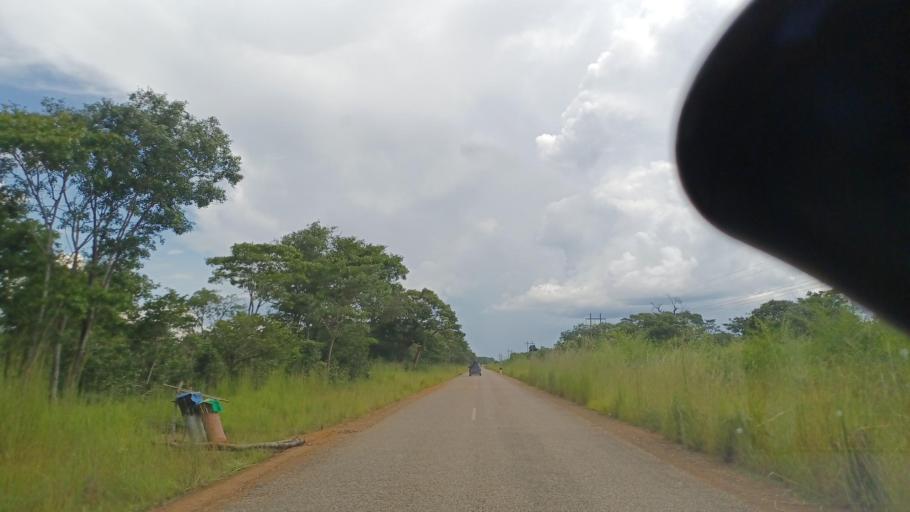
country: ZM
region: North-Western
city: Kasempa
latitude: -13.1357
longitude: 25.8771
